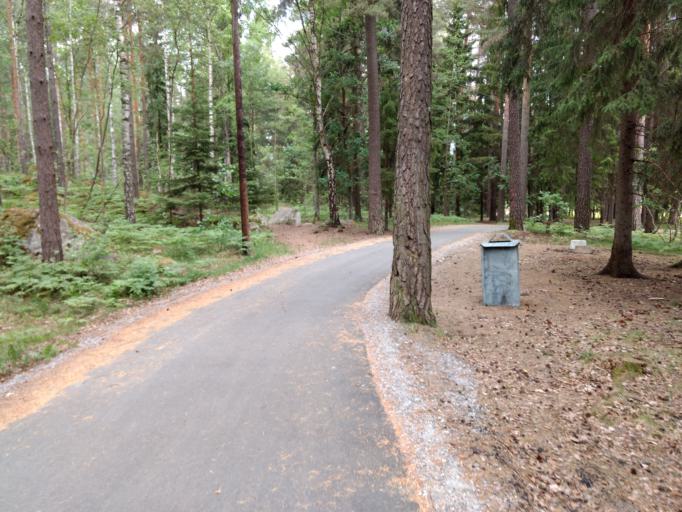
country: SE
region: Stockholm
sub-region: Upplands Vasby Kommun
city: Upplands Vaesby
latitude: 59.5314
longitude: 17.9166
